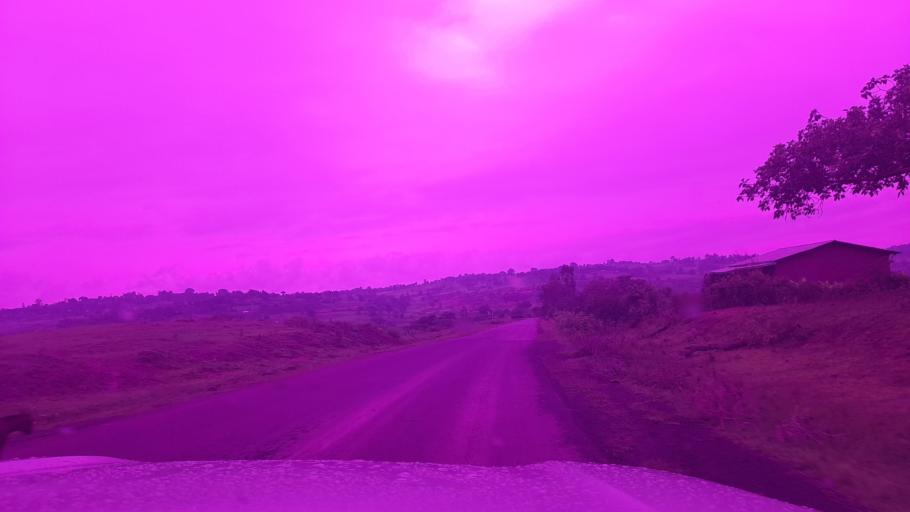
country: ET
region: Oromiya
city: Jima
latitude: 7.7318
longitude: 37.2831
